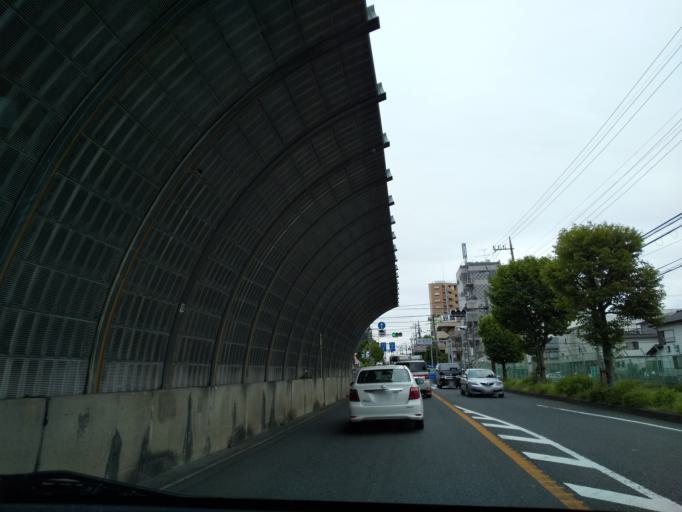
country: JP
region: Kanagawa
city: Zama
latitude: 35.5093
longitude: 139.4128
